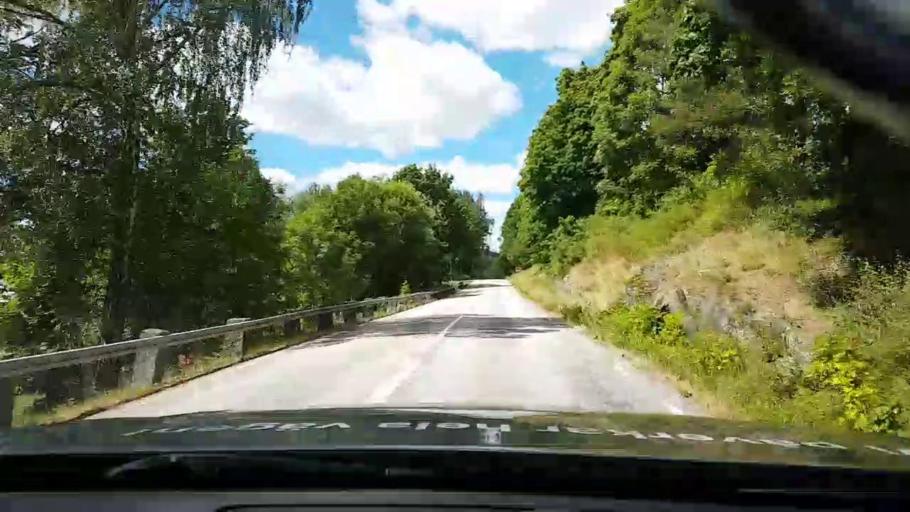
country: SE
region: Kalmar
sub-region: Vasterviks Kommun
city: Overum
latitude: 58.0731
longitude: 16.3707
